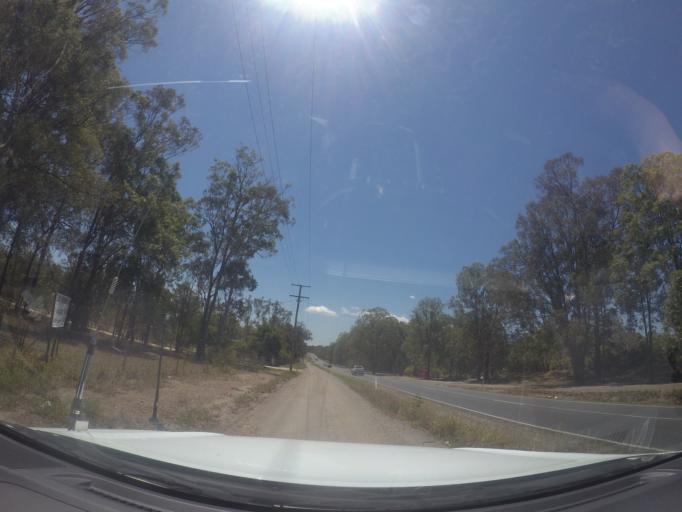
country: AU
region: Queensland
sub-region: Logan
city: Logan Reserve
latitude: -27.7407
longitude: 153.1272
